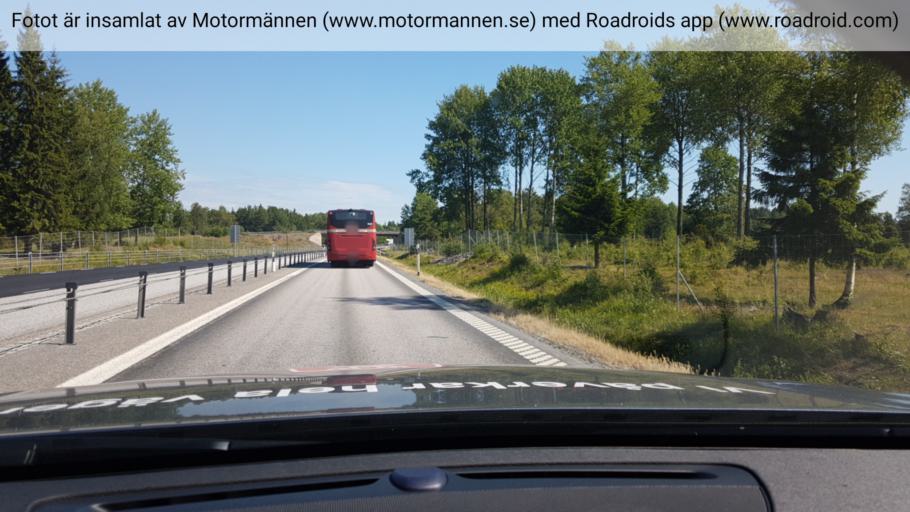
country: SE
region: Stockholm
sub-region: Osterakers Kommun
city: Akersberga
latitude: 59.6075
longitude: 18.2794
